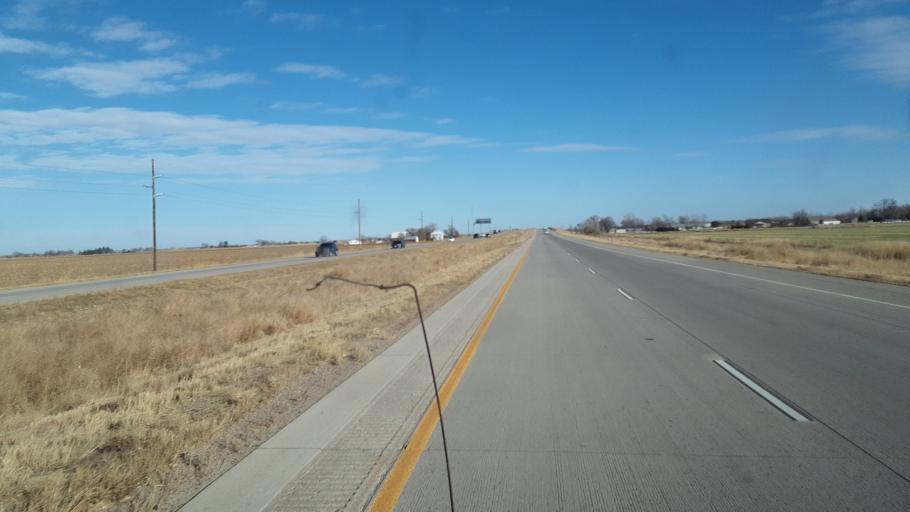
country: US
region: Colorado
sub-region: Morgan County
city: Brush
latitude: 40.2679
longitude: -103.6866
